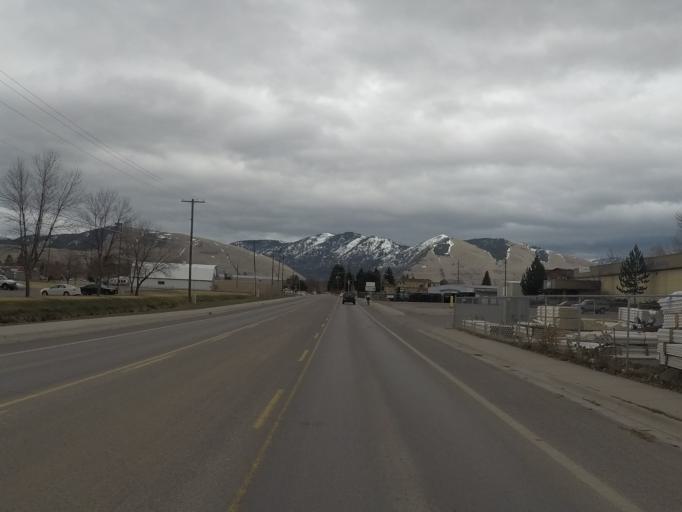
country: US
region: Montana
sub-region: Missoula County
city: Orchard Homes
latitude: 46.8815
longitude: -114.0266
